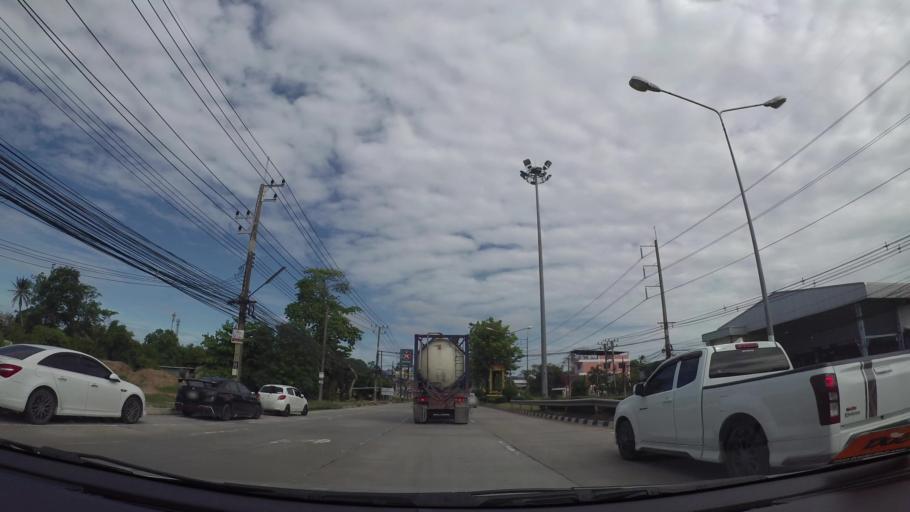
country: TH
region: Rayong
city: Ban Chang
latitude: 12.7345
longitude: 101.1320
